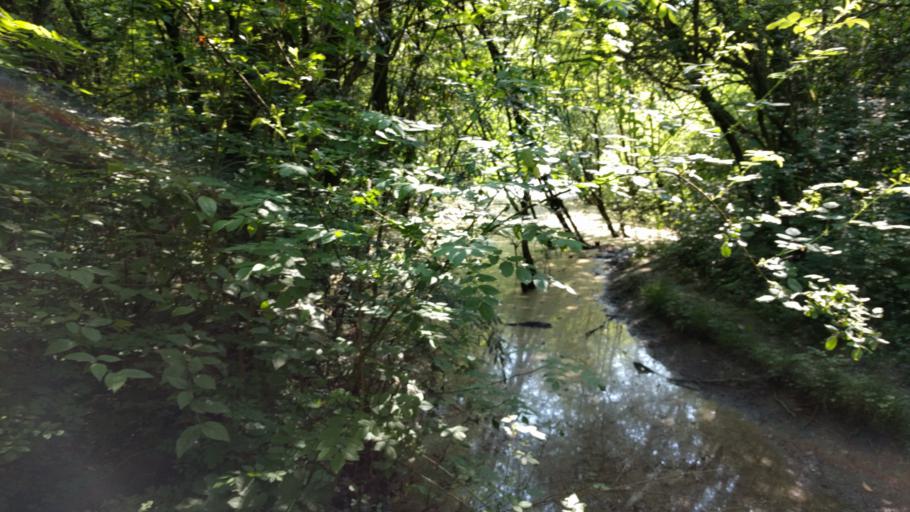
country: GB
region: England
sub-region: Warrington
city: Croft
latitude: 53.4188
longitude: -2.5316
